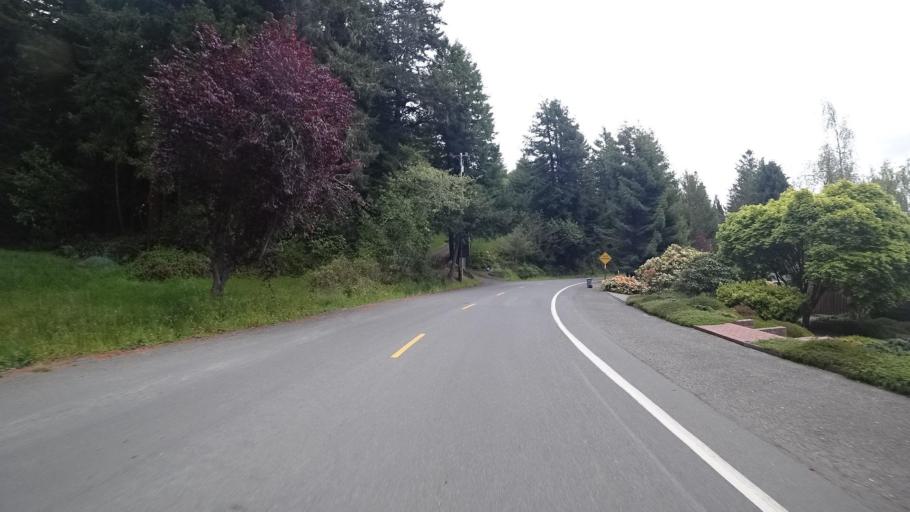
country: US
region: California
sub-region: Humboldt County
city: Bayside
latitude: 40.8490
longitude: -124.0488
